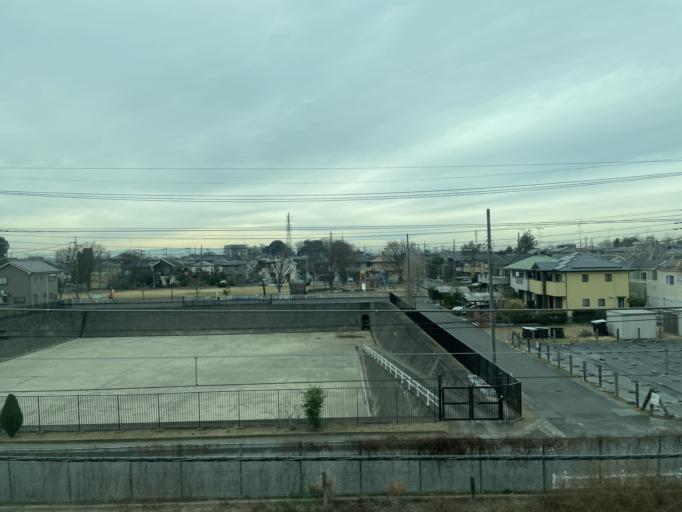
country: JP
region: Saitama
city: Kukichuo
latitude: 36.0939
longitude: 139.6792
